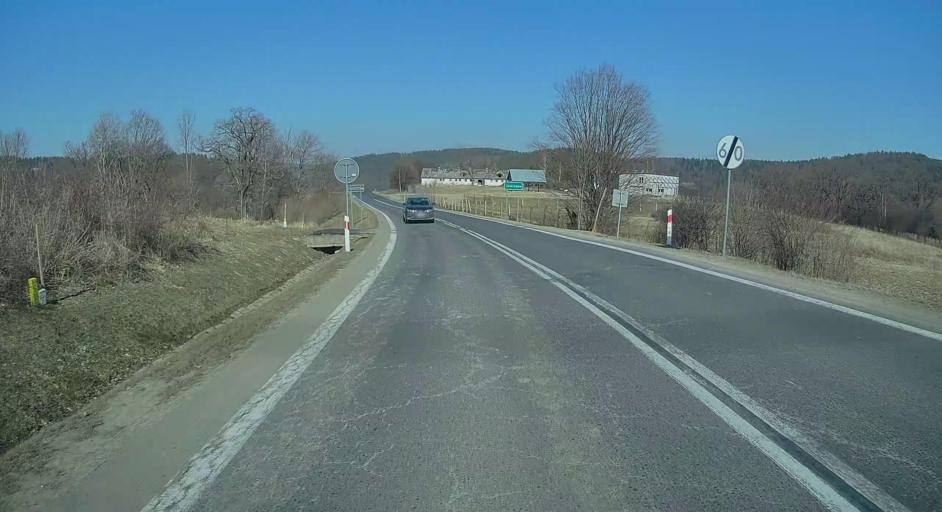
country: PL
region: Subcarpathian Voivodeship
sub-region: Powiat przemyski
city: Bircza
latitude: 49.6558
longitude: 22.4293
